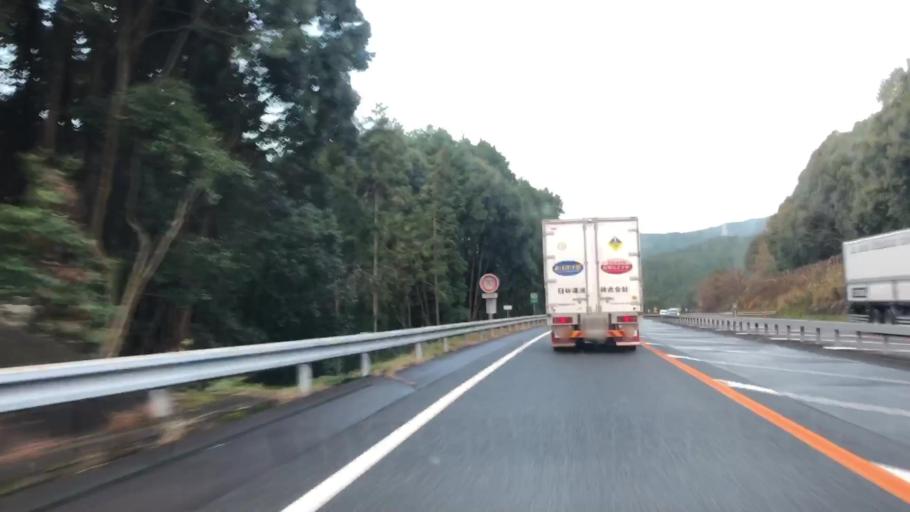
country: JP
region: Saga Prefecture
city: Imaricho-ko
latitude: 33.1546
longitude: 129.8842
